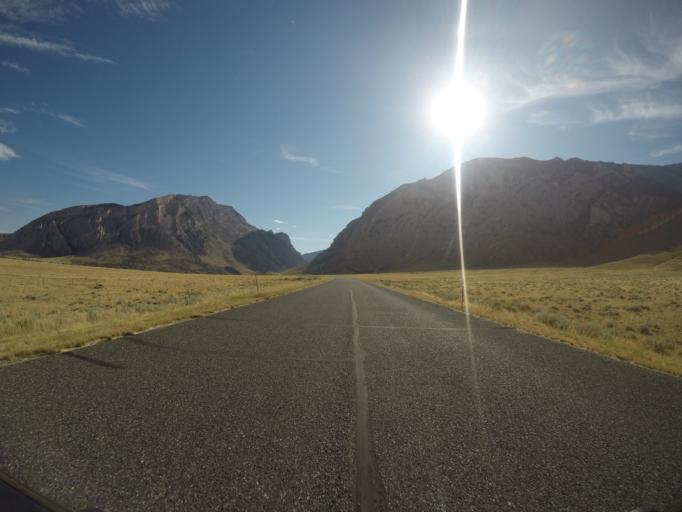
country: US
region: Montana
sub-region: Carbon County
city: Red Lodge
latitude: 44.8630
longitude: -109.2858
